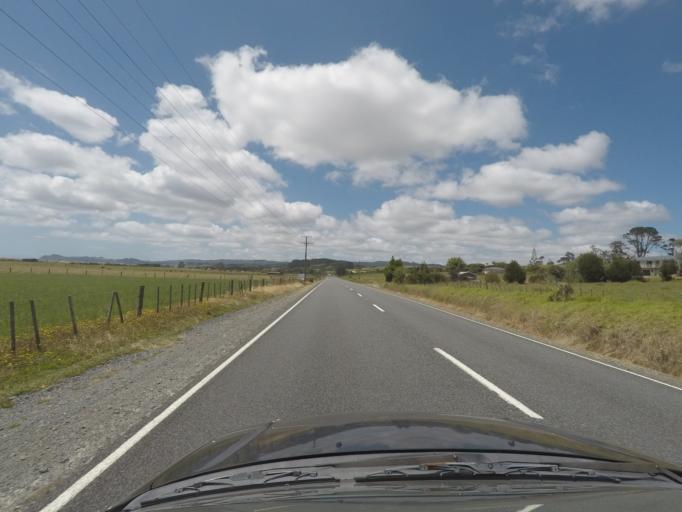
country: NZ
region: Northland
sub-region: Whangarei
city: Ruakaka
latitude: -36.0069
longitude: 174.4793
